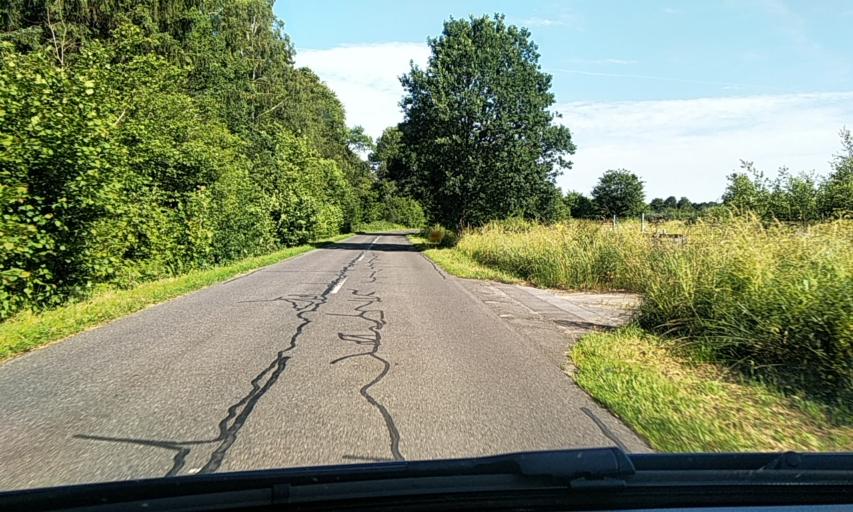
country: DE
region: Schleswig-Holstein
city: Fockbek
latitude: 54.2780
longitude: 9.5744
